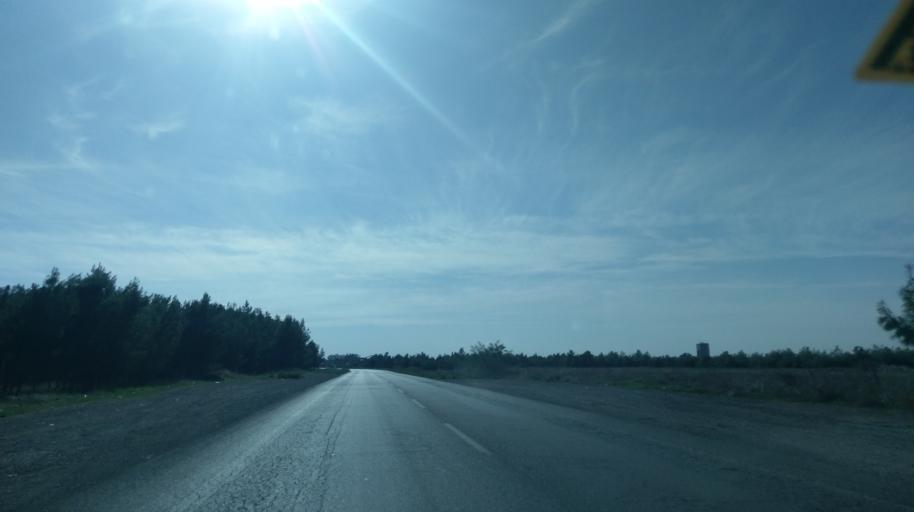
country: CY
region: Ammochostos
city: Trikomo
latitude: 35.2968
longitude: 33.9354
